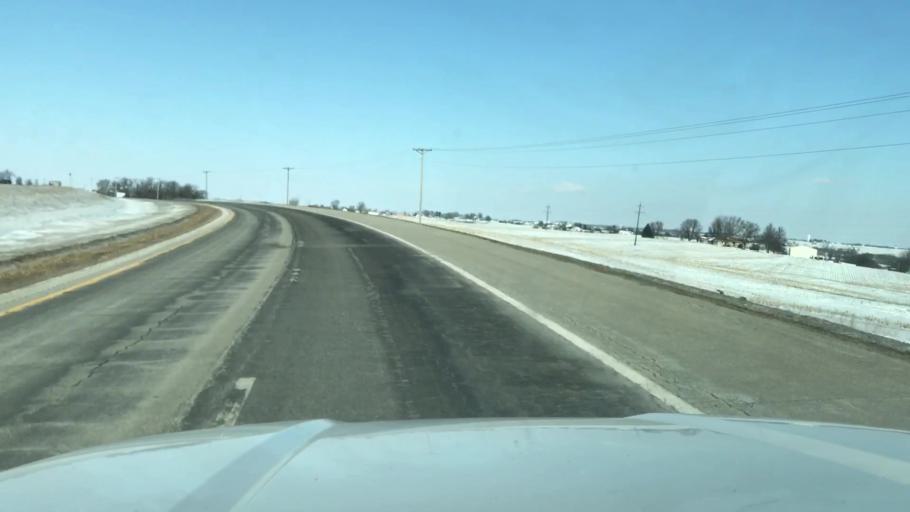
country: US
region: Missouri
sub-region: Nodaway County
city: Maryville
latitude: 40.2726
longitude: -94.8673
